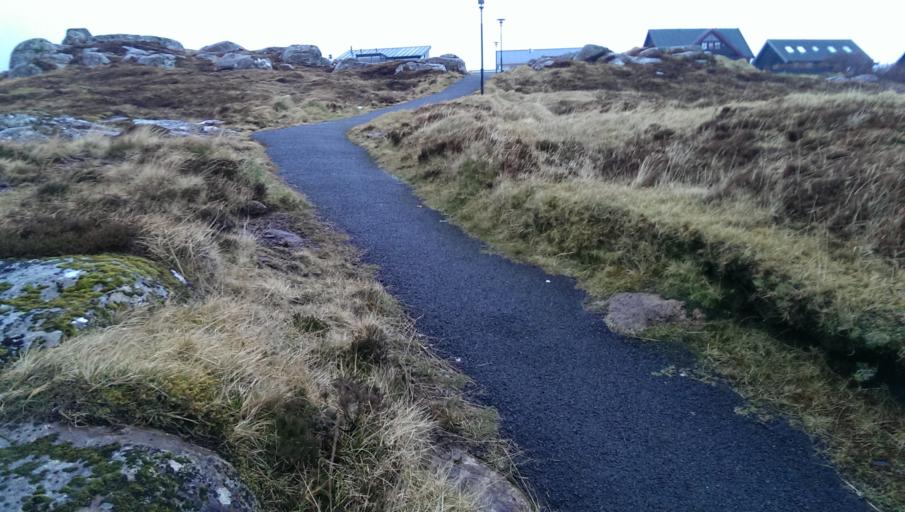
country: FO
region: Streymoy
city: Hoyvik
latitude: 62.0307
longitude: -6.7855
